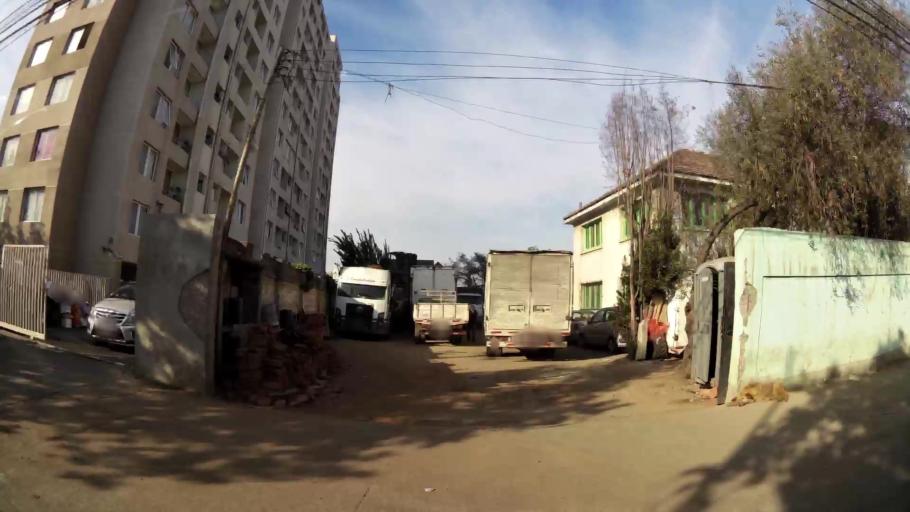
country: CL
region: Santiago Metropolitan
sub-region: Provincia de Santiago
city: Santiago
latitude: -33.5147
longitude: -70.6661
